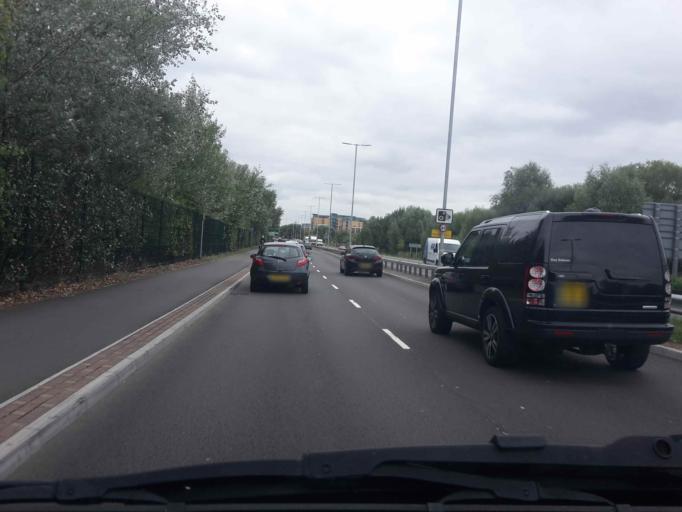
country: GB
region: England
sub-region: Reading
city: Reading
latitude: 51.4277
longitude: -0.9808
